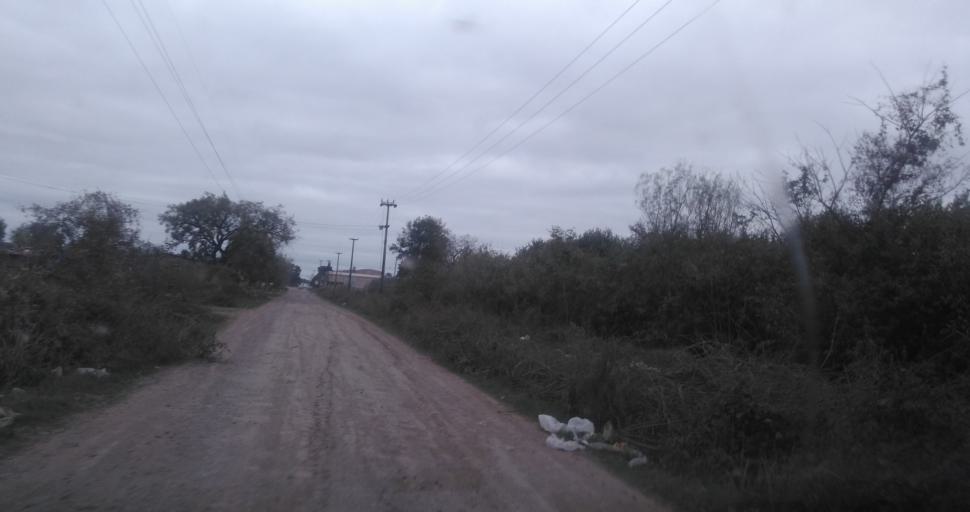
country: AR
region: Chaco
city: Fontana
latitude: -27.4289
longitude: -59.0210
